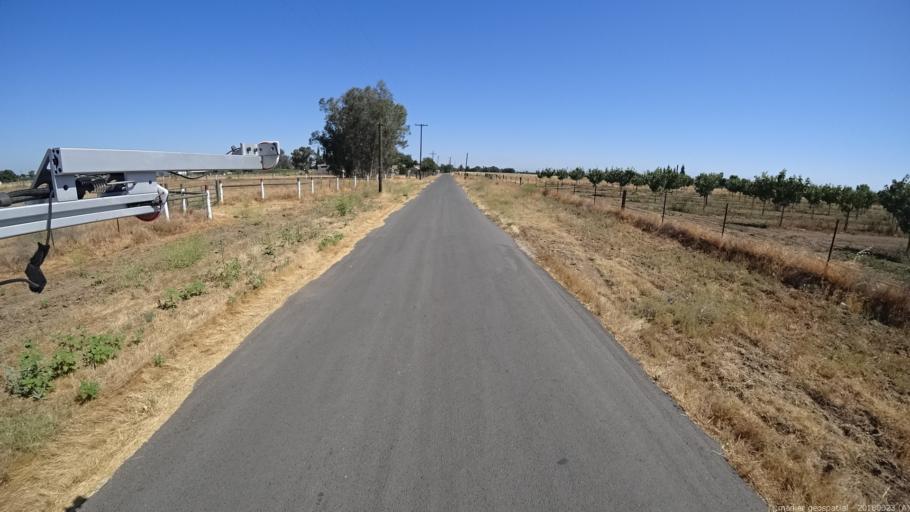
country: US
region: California
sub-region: Madera County
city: Parksdale
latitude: 36.9792
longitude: -120.0106
